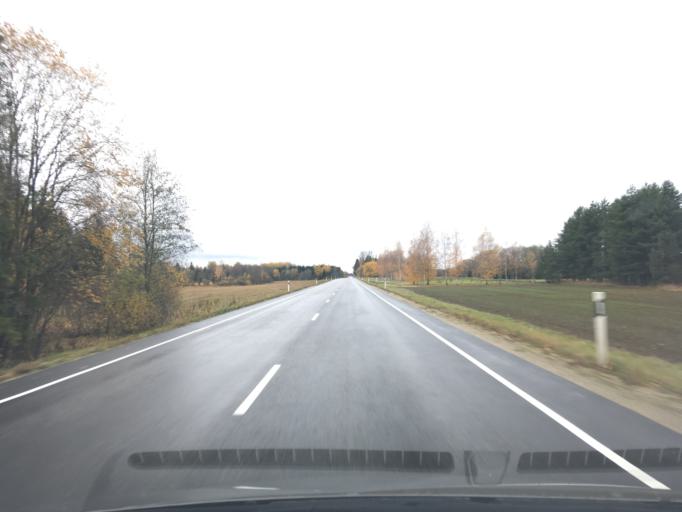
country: EE
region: Jogevamaa
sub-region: Tabivere vald
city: Tabivere
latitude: 58.4463
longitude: 26.5133
